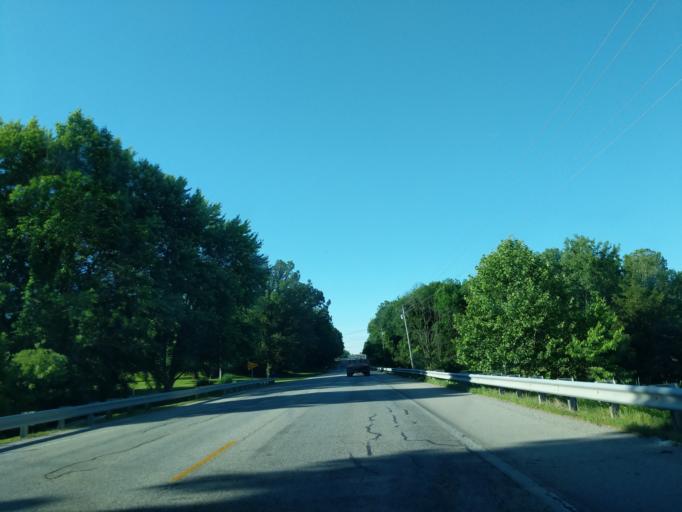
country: US
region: Indiana
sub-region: Shelby County
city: Morristown
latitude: 39.6687
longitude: -85.7731
